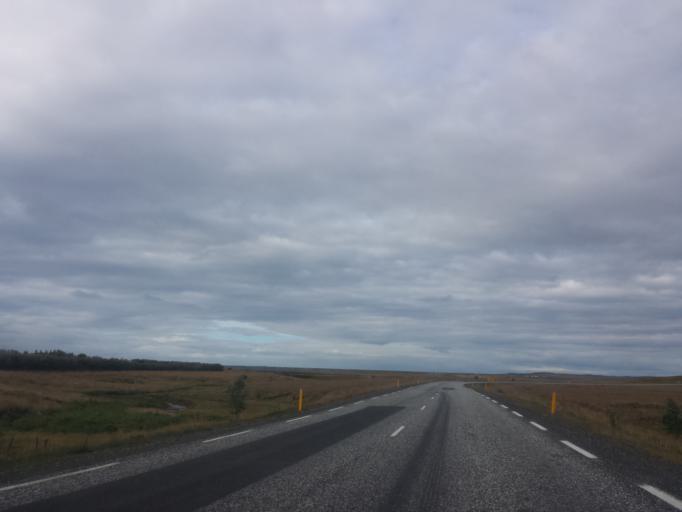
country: IS
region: West
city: Borgarnes
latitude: 64.3743
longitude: -21.8433
